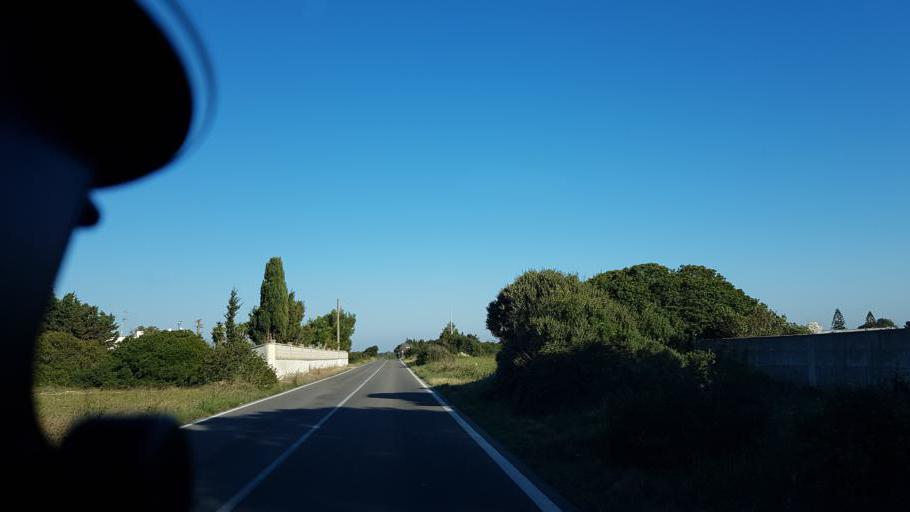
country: IT
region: Apulia
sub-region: Provincia di Lecce
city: Struda
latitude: 40.3937
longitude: 18.2739
